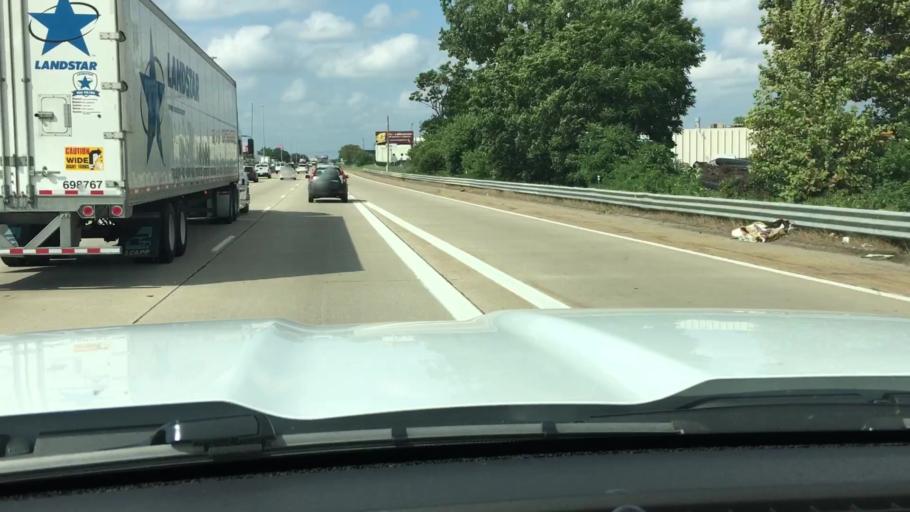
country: US
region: Michigan
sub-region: Kent County
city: Cutlerville
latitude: 42.8699
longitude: -85.6796
